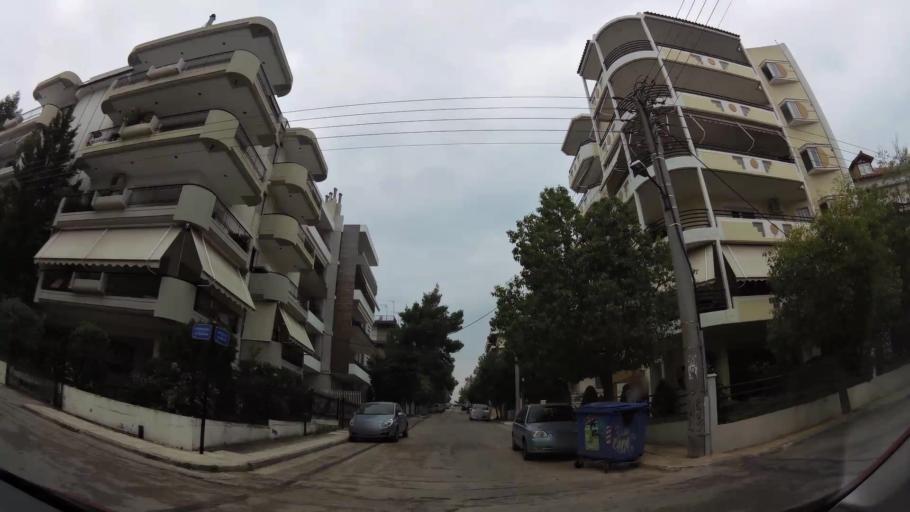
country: GR
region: Attica
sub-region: Nomarchia Athinas
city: Ilion
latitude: 38.0370
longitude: 23.7099
